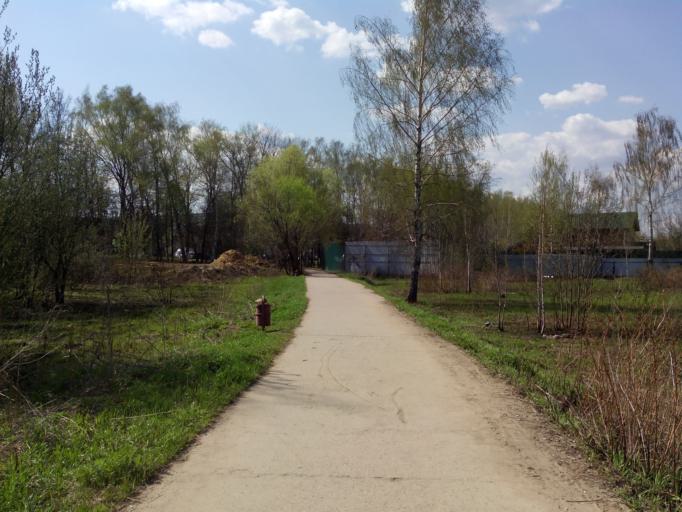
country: RU
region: Moskovskaya
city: Odintsovo
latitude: 55.6667
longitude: 37.2493
